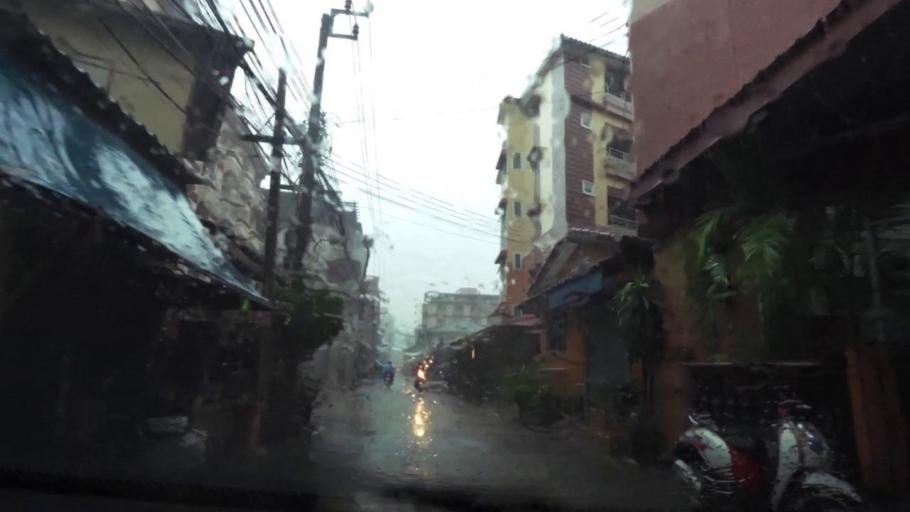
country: TH
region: Bangkok
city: Phra Khanong
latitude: 13.7170
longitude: 100.5987
